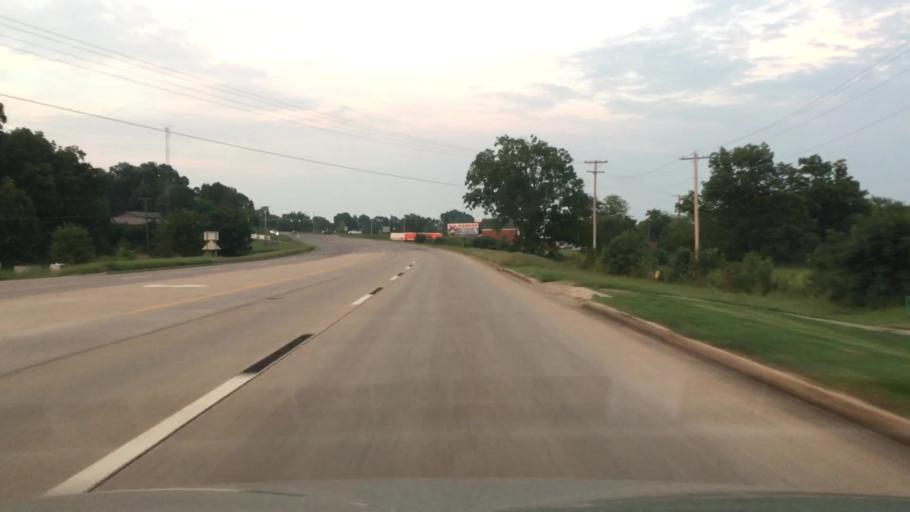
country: US
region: Oklahoma
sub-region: Cherokee County
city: Park Hill
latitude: 35.8560
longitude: -94.9835
